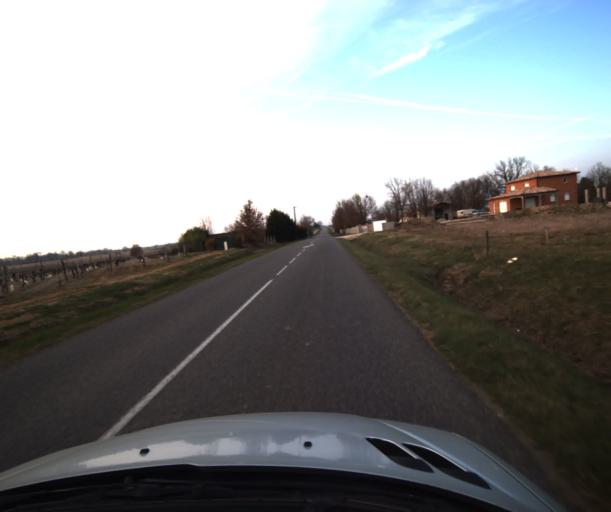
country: FR
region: Midi-Pyrenees
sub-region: Departement du Tarn-et-Garonne
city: Labastide-Saint-Pierre
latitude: 43.8852
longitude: 1.3755
